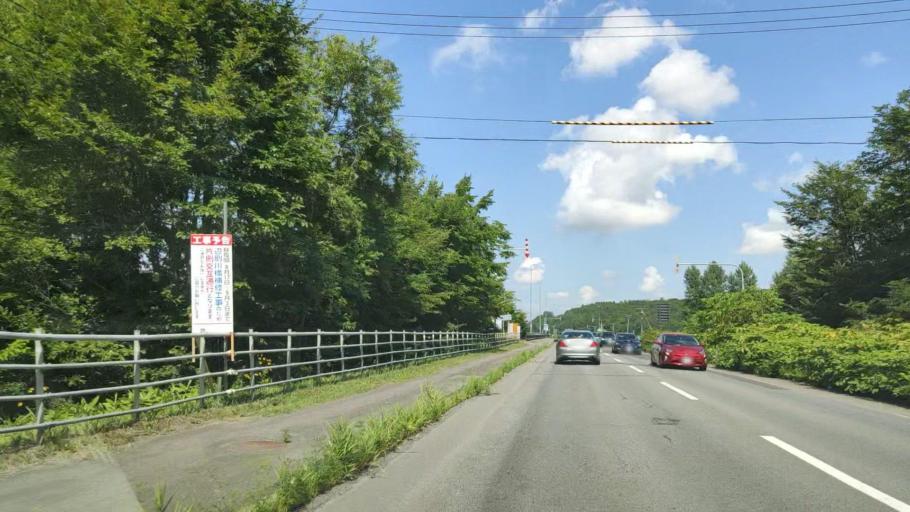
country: JP
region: Hokkaido
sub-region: Asahikawa-shi
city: Asahikawa
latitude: 43.6239
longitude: 142.4675
